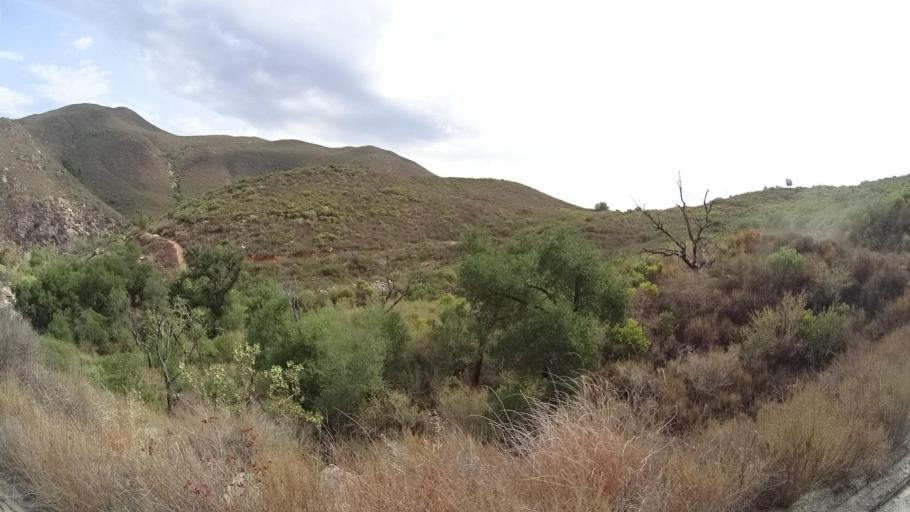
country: US
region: California
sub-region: San Diego County
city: Ramona
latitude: 33.1208
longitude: -116.7922
